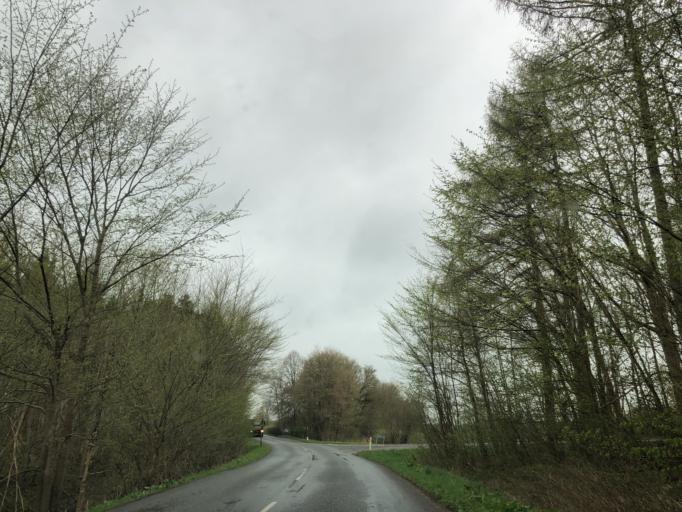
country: DK
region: Zealand
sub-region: Lejre Kommune
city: Kirke Hvalso
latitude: 55.5276
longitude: 11.8588
